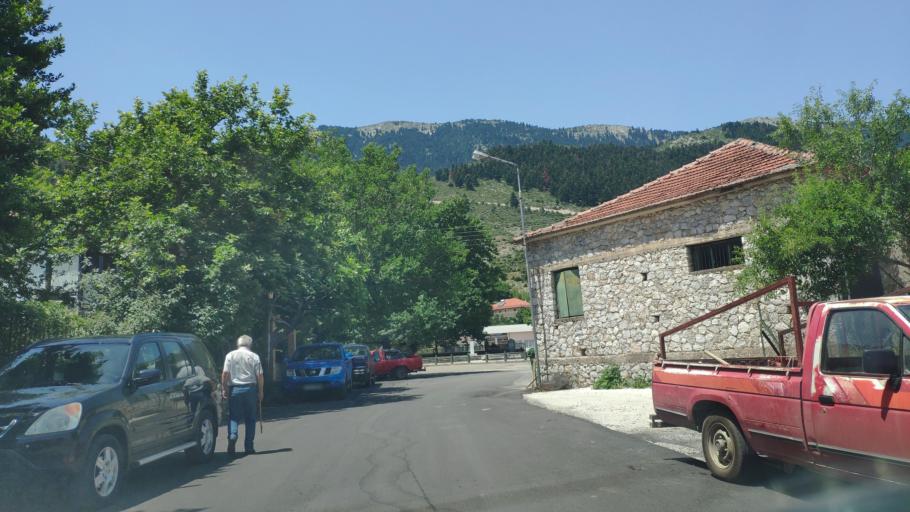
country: GR
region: West Greece
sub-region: Nomos Aitolias kai Akarnanias
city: Krikellos
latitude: 39.0503
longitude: 21.3619
